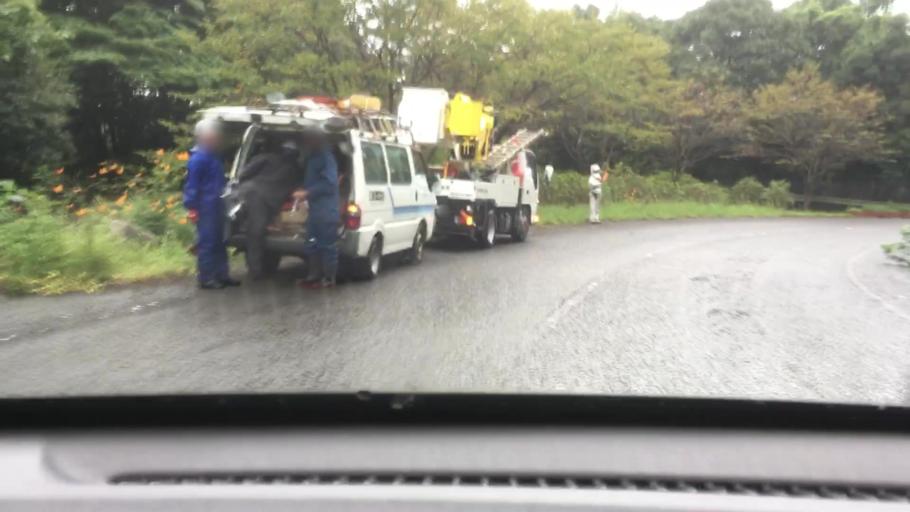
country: JP
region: Nagasaki
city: Togitsu
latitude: 32.8744
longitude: 129.7620
